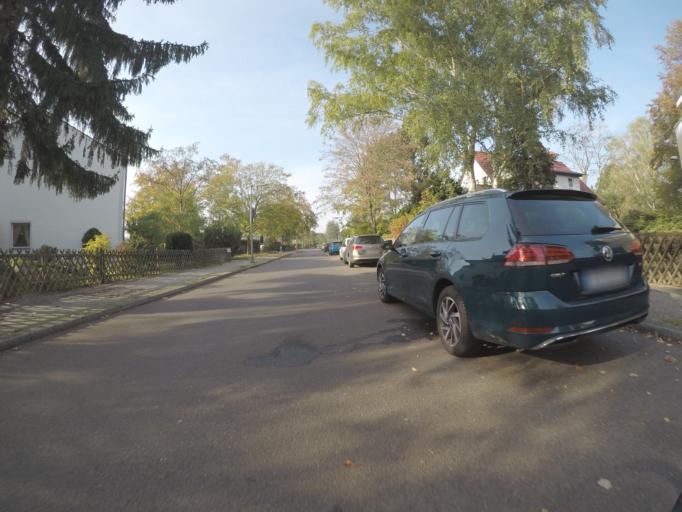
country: DE
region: Berlin
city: Britz
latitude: 52.4223
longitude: 13.4254
